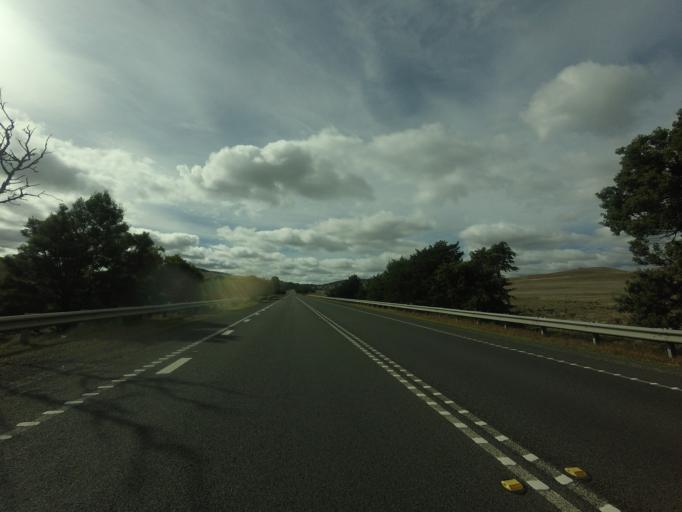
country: AU
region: Tasmania
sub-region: Brighton
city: Bridgewater
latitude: -42.4651
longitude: 147.1863
